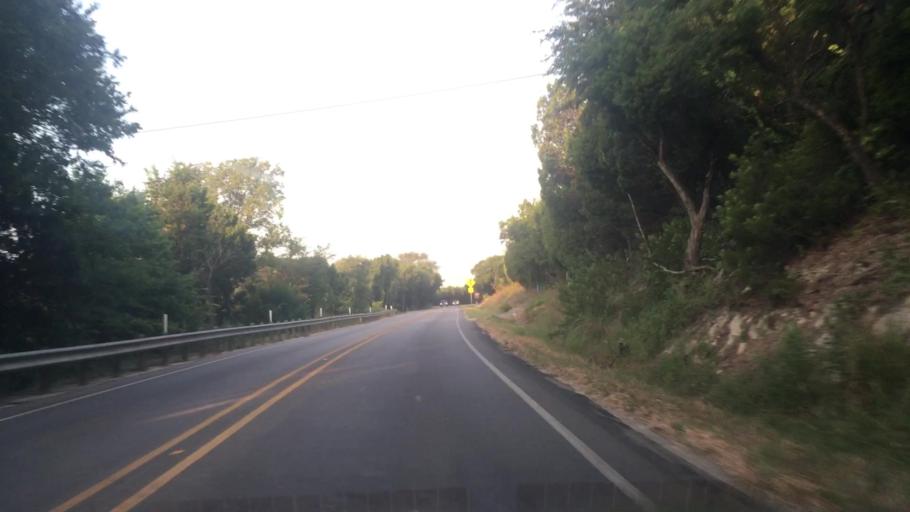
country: US
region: Texas
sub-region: Williamson County
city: Anderson Mill
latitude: 30.4443
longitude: -97.8630
